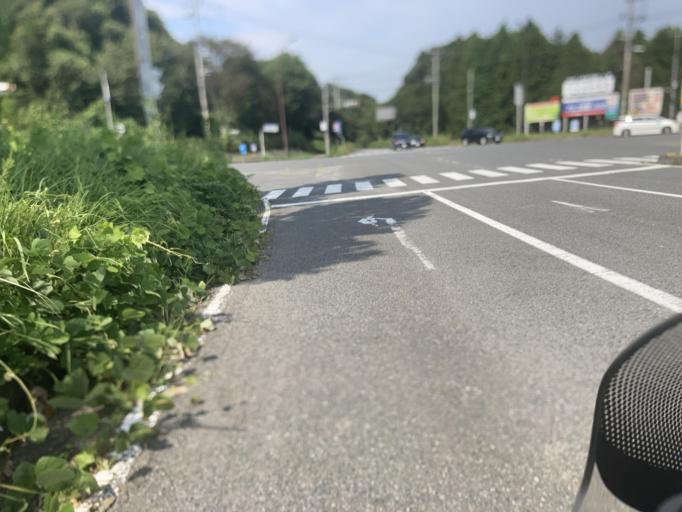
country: JP
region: Fukushima
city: Iwaki
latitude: 37.0171
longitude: 140.9221
